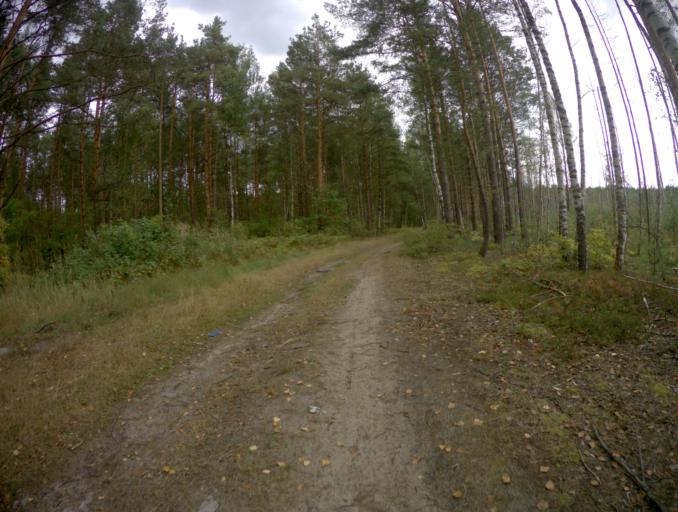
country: RU
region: Vladimir
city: Raduzhnyy
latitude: 56.0369
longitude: 40.3709
